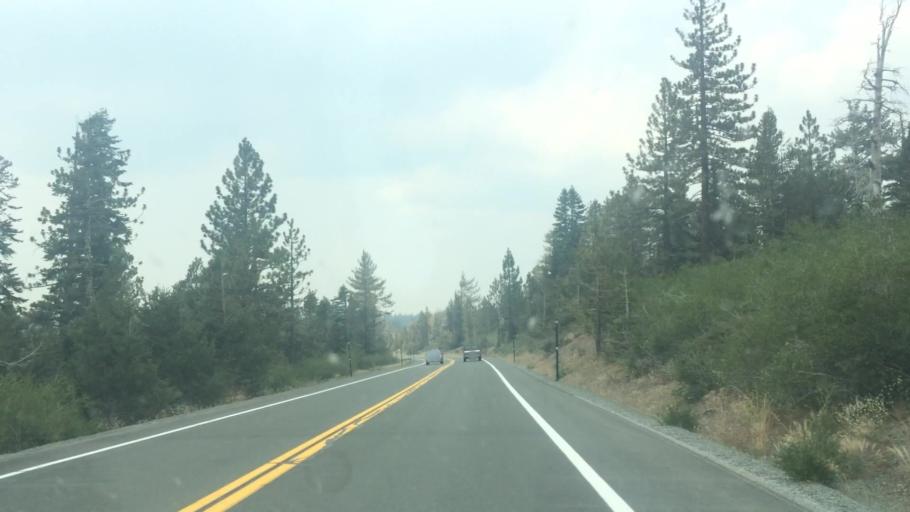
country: US
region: California
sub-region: El Dorado County
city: South Lake Tahoe
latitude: 38.6327
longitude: -120.1629
